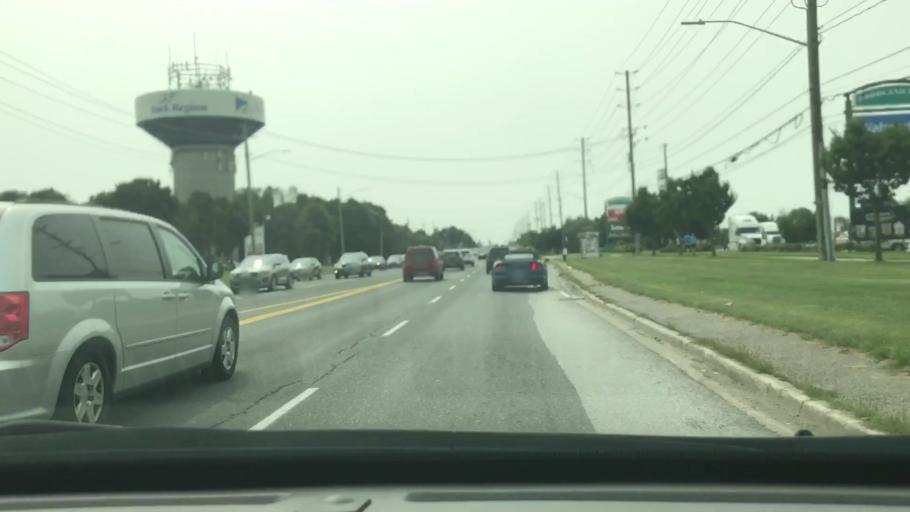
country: CA
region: Ontario
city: Newmarket
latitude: 44.0676
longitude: -79.4836
